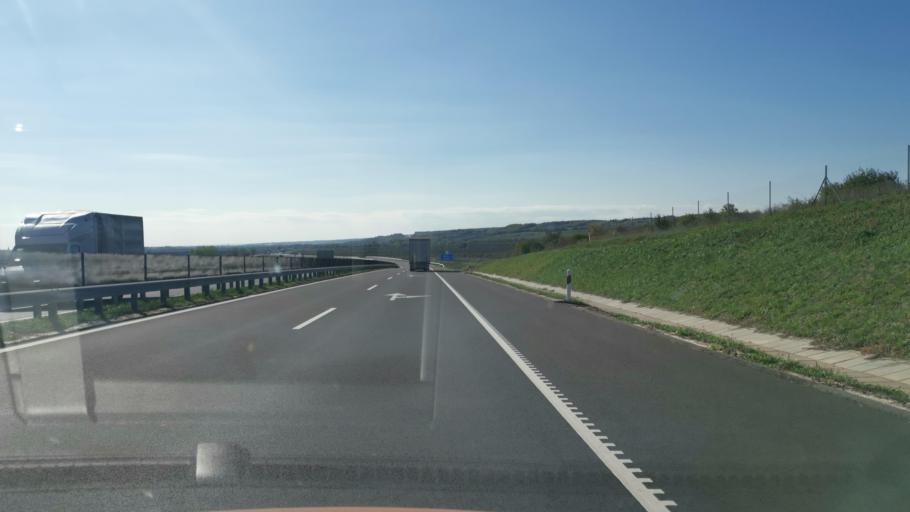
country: HU
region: Borsod-Abauj-Zemplen
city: Halmaj
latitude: 48.2584
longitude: 20.9840
